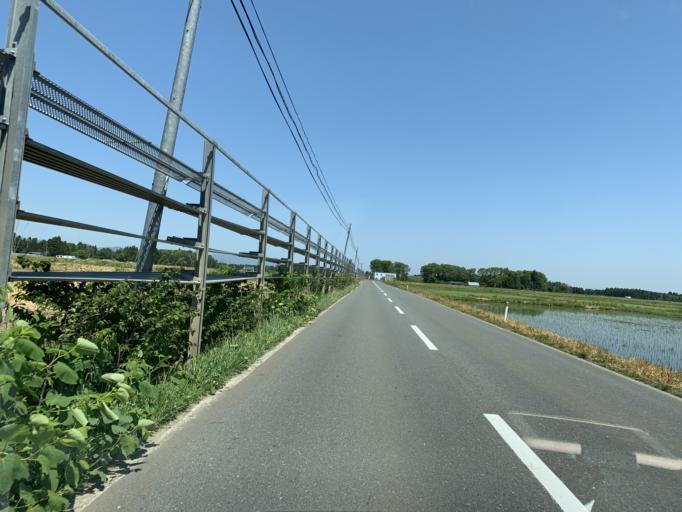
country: JP
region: Iwate
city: Kitakami
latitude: 39.2562
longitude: 141.0647
